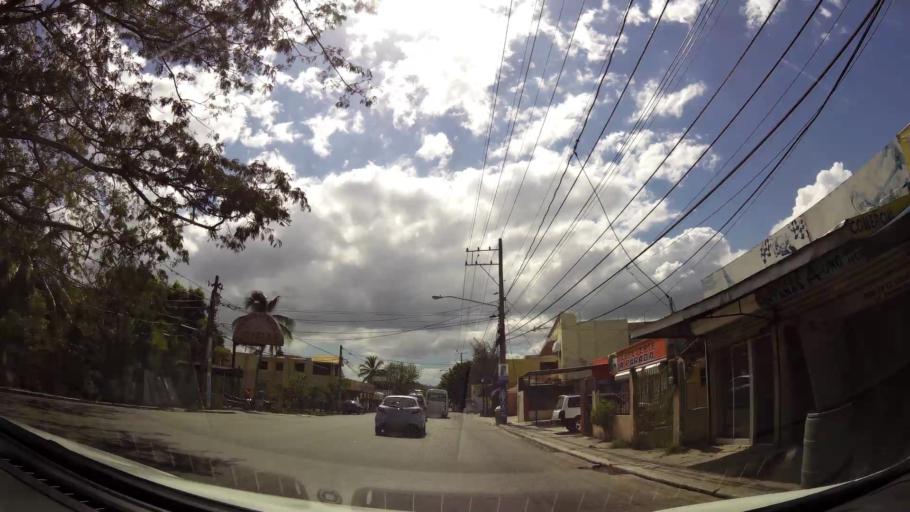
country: DO
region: San Cristobal
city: San Cristobal
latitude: 18.4195
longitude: -70.1025
